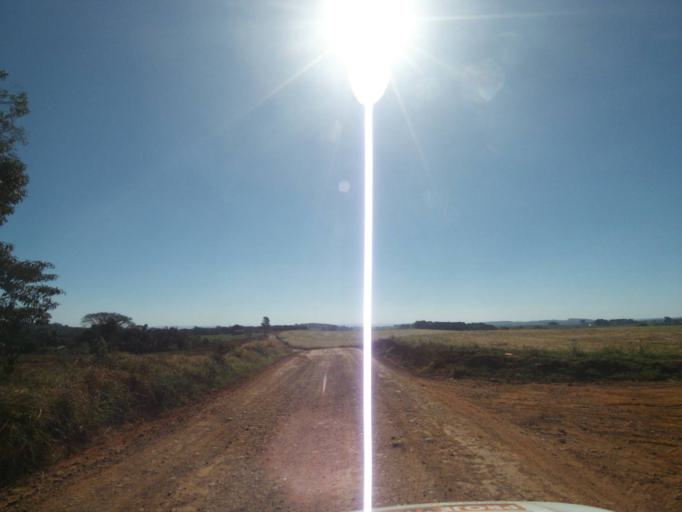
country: BR
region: Parana
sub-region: Tibagi
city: Tibagi
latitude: -24.5839
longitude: -50.6105
